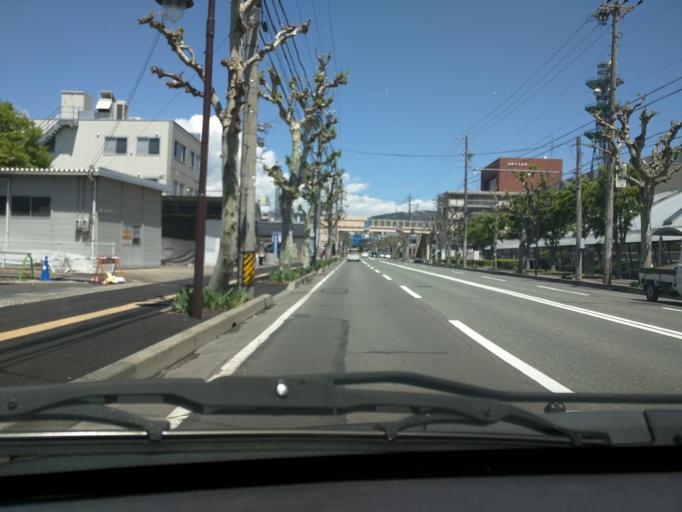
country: JP
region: Nagano
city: Nagano-shi
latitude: 36.6448
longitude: 138.1987
